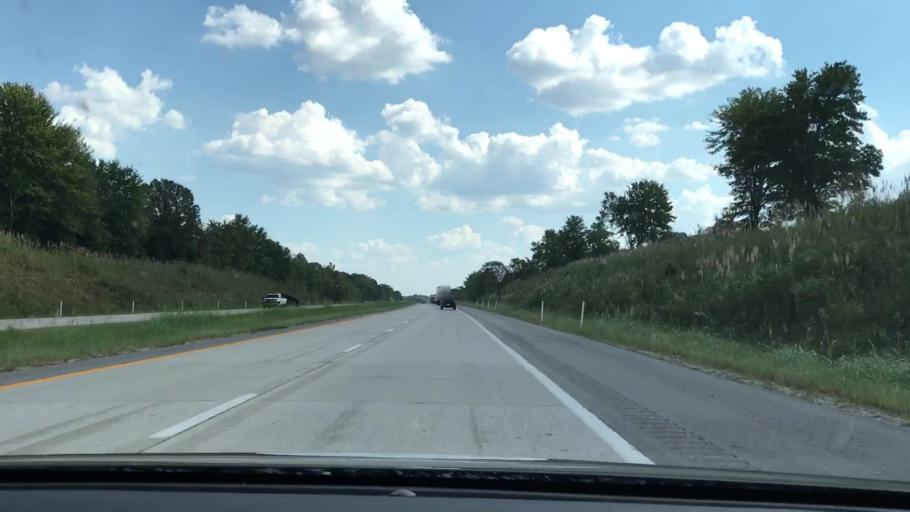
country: US
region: Kentucky
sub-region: Ohio County
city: Oak Grove
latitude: 37.3667
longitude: -86.7983
